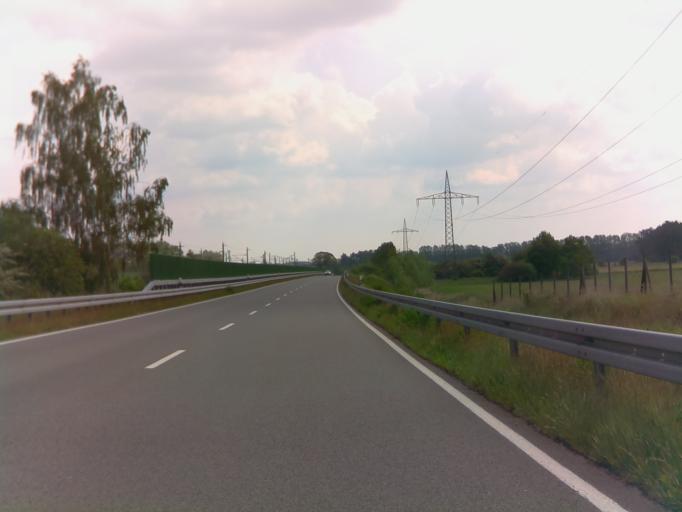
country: DE
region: Brandenburg
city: Rathenow
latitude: 52.5903
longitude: 12.2609
